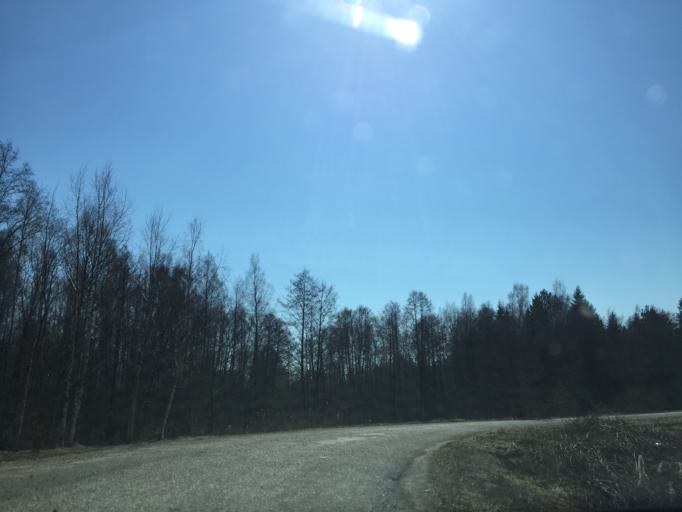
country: EE
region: Jogevamaa
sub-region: Mustvee linn
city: Mustvee
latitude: 58.7709
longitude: 26.9490
